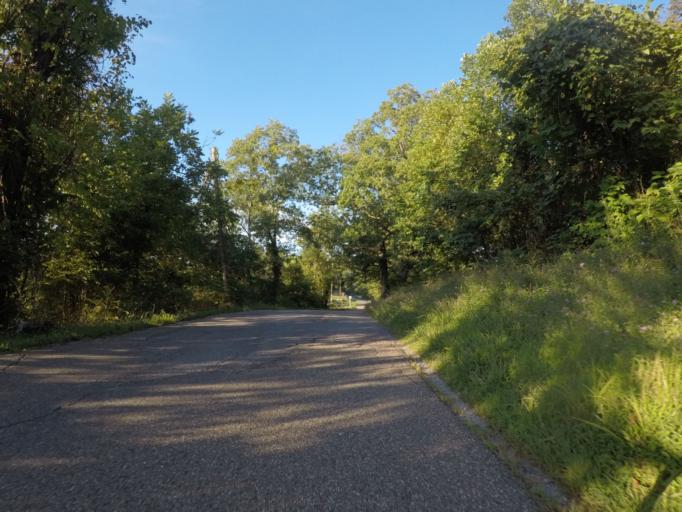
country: US
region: Ohio
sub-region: Lawrence County
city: Coal Grove
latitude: 38.5907
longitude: -82.5494
